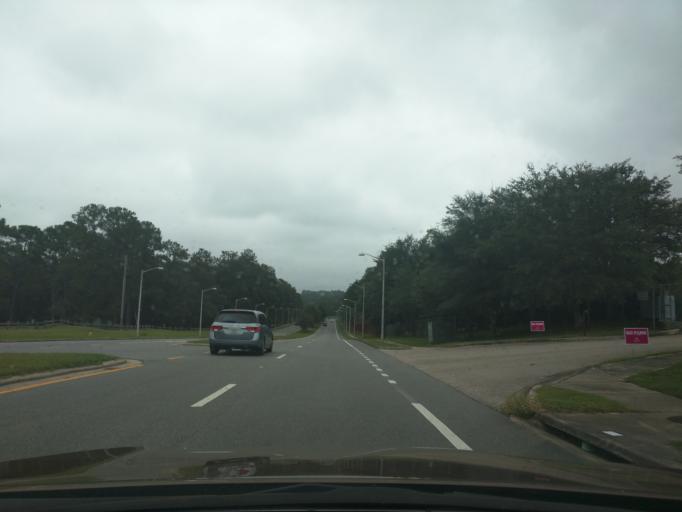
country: US
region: Florida
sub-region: Leon County
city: Tallahassee
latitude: 30.4400
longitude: -84.2157
